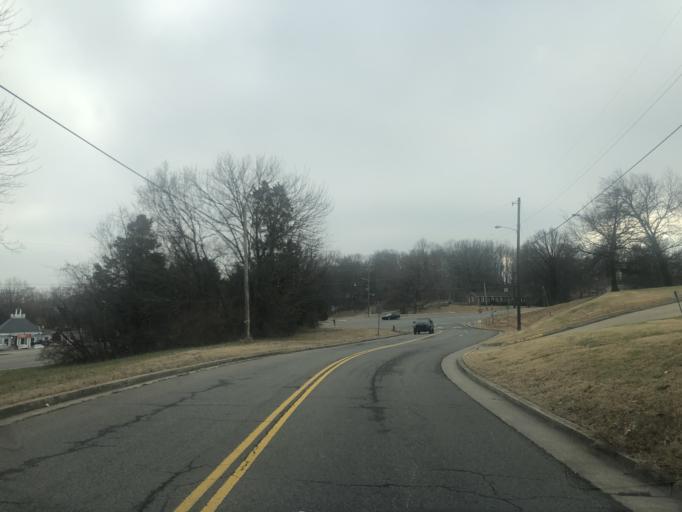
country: US
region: Tennessee
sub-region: Rutherford County
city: La Vergne
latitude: 36.0644
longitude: -86.6381
